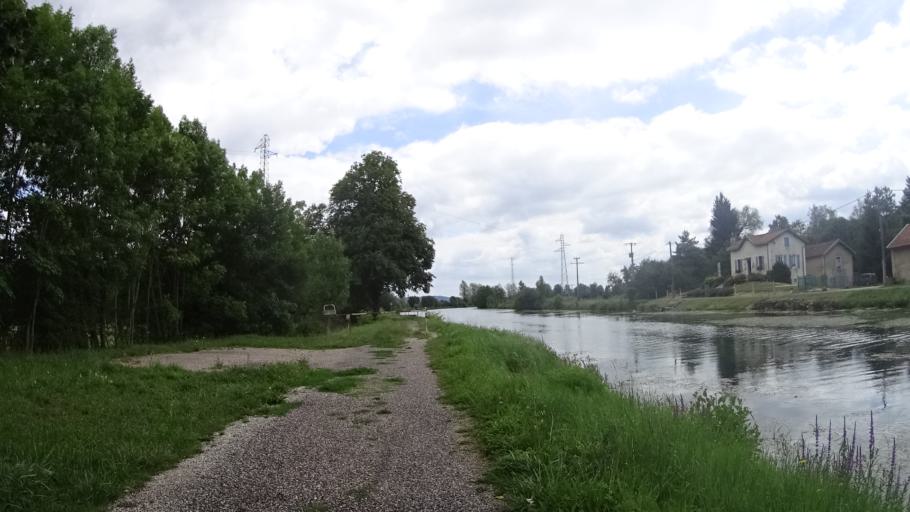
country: FR
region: Lorraine
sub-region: Departement de la Meuse
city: Commercy
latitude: 48.7571
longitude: 5.6048
